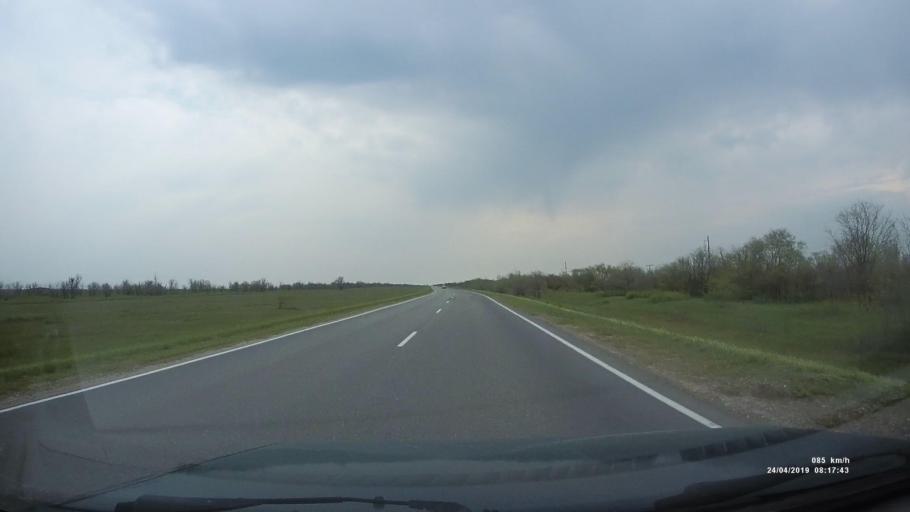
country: RU
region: Kalmykiya
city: Priyutnoye
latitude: 46.0980
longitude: 43.6357
